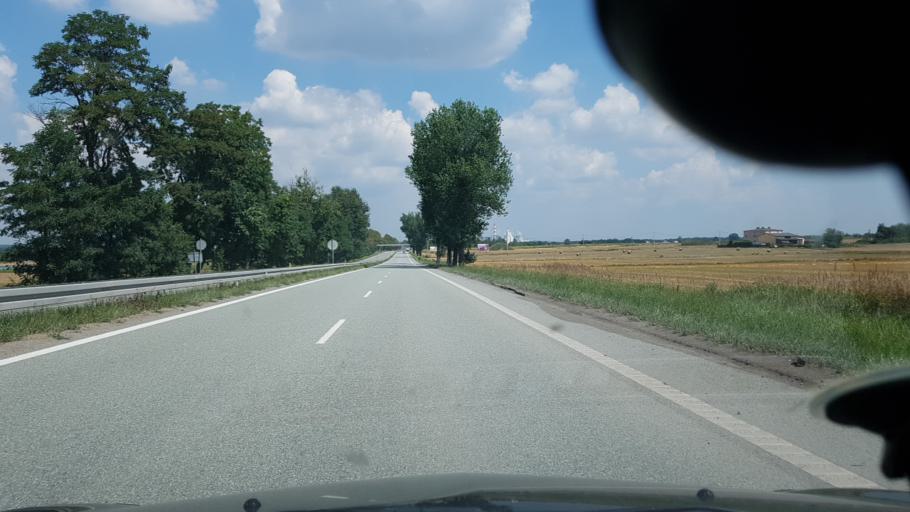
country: PL
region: Silesian Voivodeship
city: Gardawice
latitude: 50.1000
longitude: 18.7767
